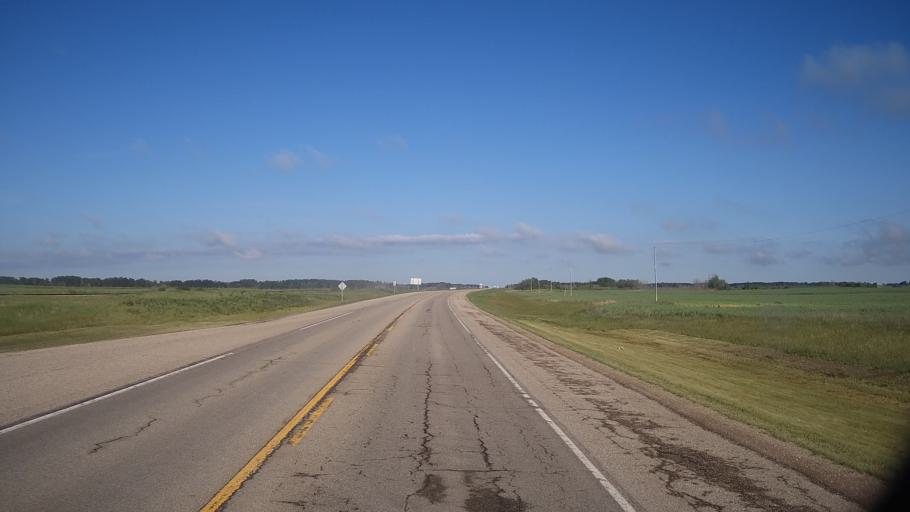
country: CA
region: Saskatchewan
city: Lanigan
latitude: 51.8499
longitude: -105.0578
